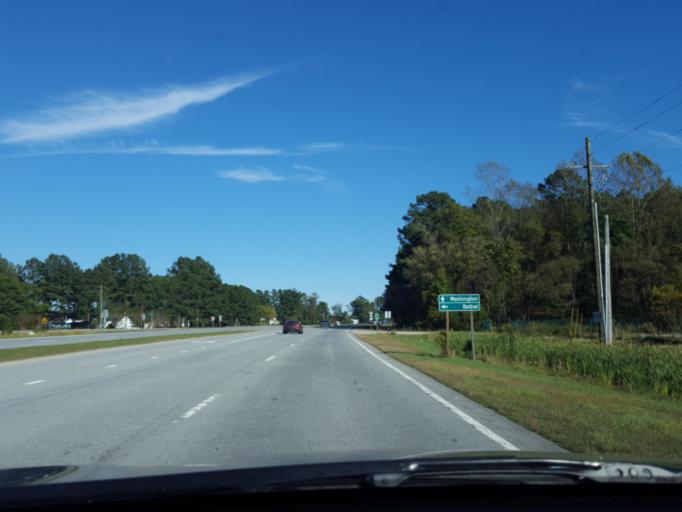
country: US
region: North Carolina
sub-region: Pitt County
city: Greenville
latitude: 35.6265
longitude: -77.2060
